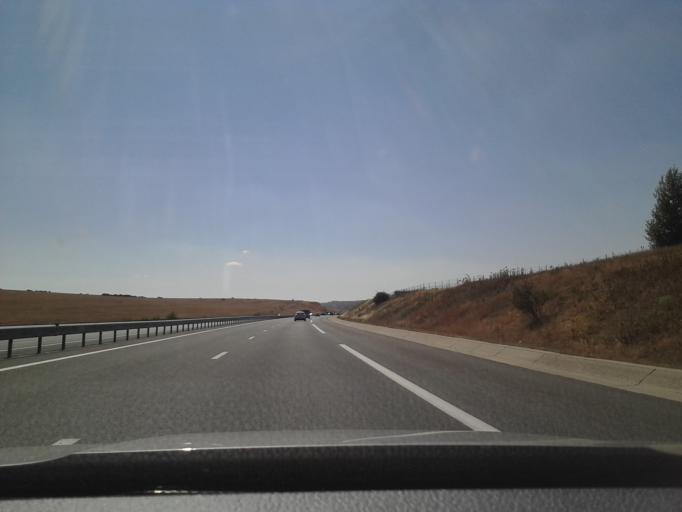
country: FR
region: Midi-Pyrenees
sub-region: Departement de l'Aveyron
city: La Cavalerie
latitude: 44.0256
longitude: 3.1153
